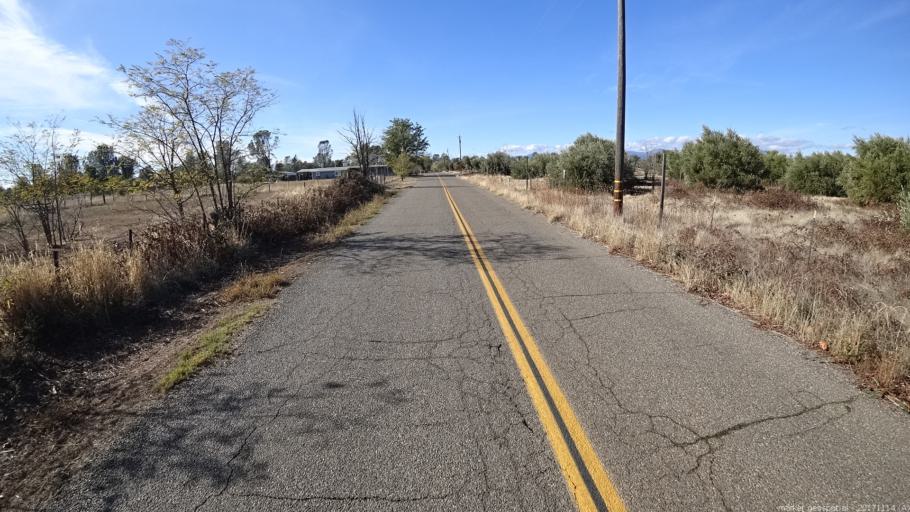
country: US
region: California
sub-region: Shasta County
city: Anderson
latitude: 40.4320
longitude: -122.4235
